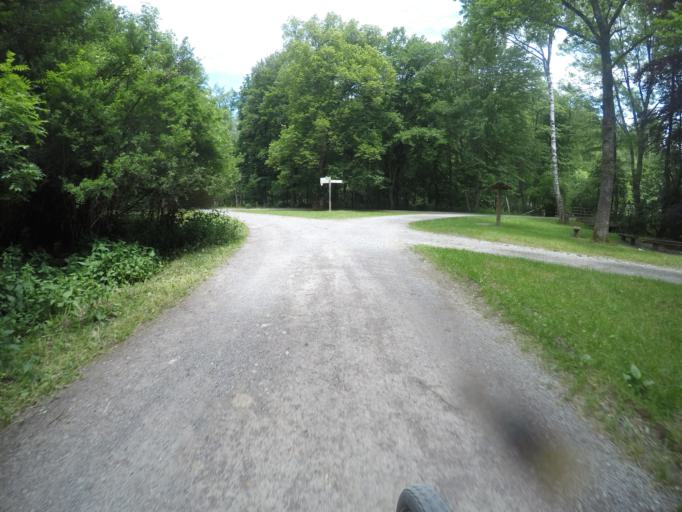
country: DE
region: Baden-Wuerttemberg
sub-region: Regierungsbezirk Stuttgart
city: Hildrizhausen
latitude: 48.5912
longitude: 8.9766
